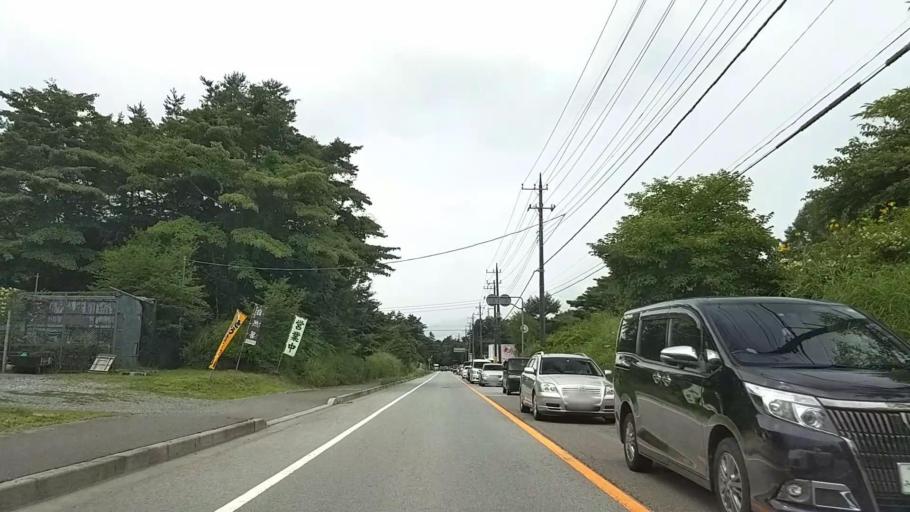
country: JP
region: Yamanashi
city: Fujikawaguchiko
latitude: 35.4779
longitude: 138.6709
